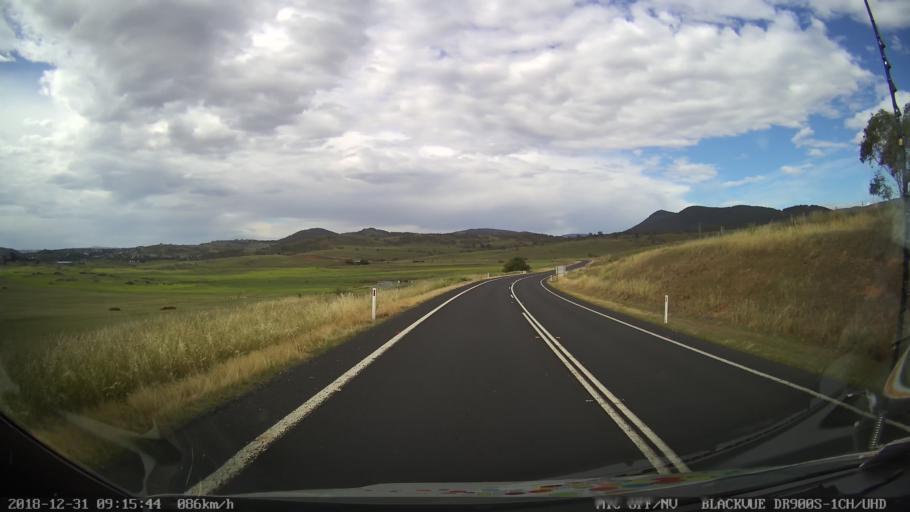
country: AU
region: New South Wales
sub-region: Snowy River
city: Jindabyne
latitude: -36.3888
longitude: 148.5983
